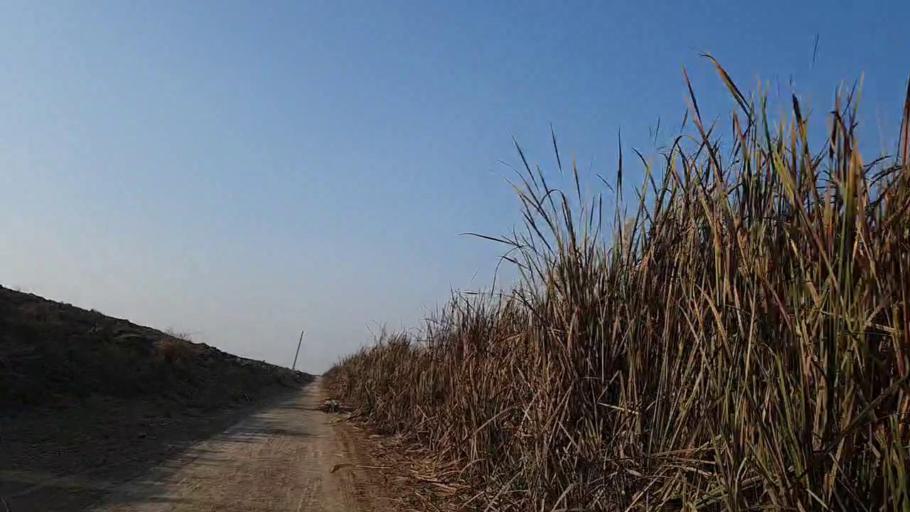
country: PK
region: Sindh
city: Sakrand
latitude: 26.0973
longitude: 68.3702
